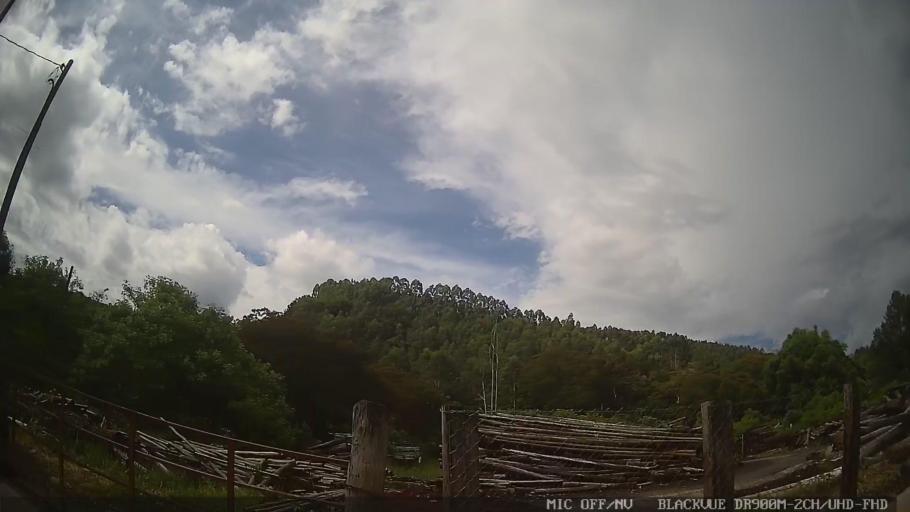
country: BR
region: Sao Paulo
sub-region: Santa Branca
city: Santa Branca
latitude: -23.5292
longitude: -45.8406
